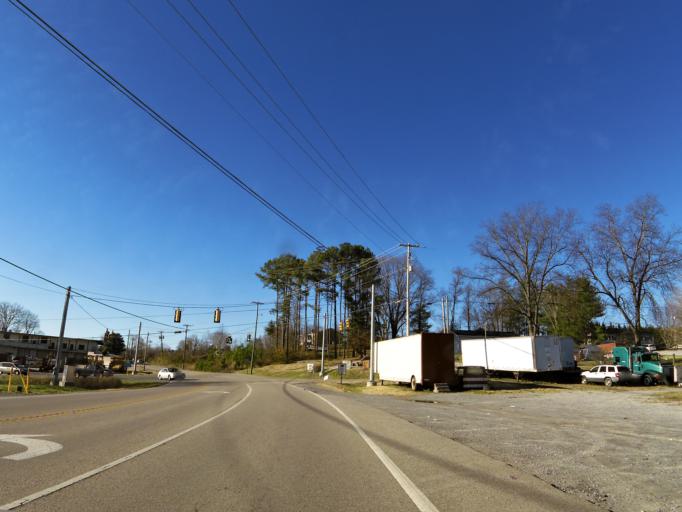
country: US
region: Tennessee
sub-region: Knox County
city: Knoxville
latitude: 36.0377
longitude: -84.0021
